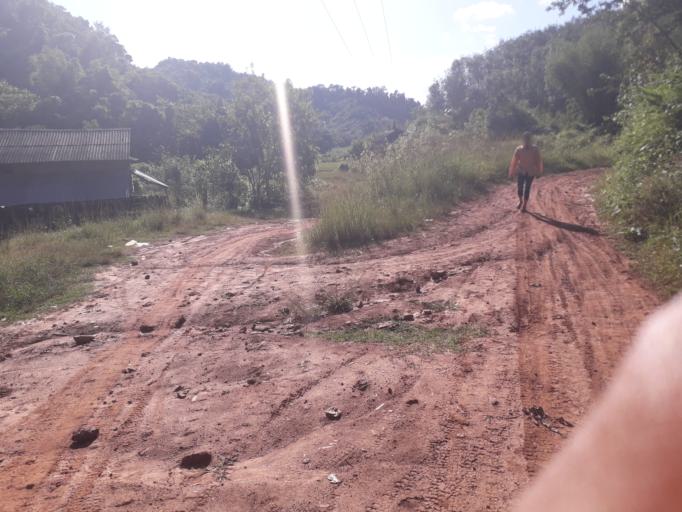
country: CN
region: Yunnan
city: Menglie
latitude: 22.1138
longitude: 101.7230
